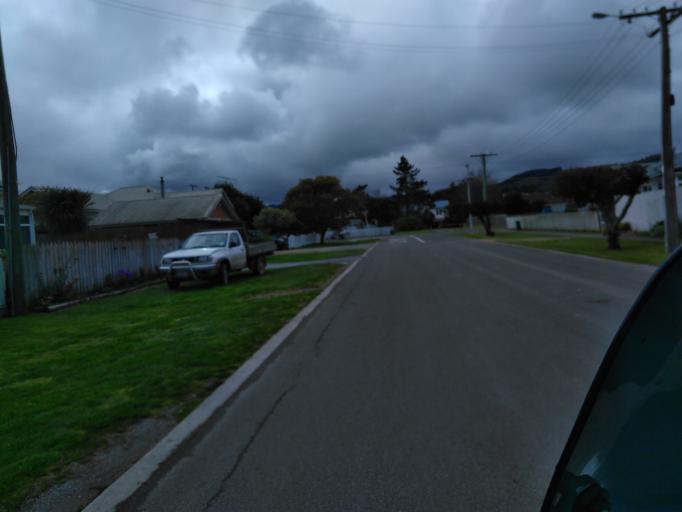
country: NZ
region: Gisborne
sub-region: Gisborne District
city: Gisborne
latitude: -38.6521
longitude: 178.0088
